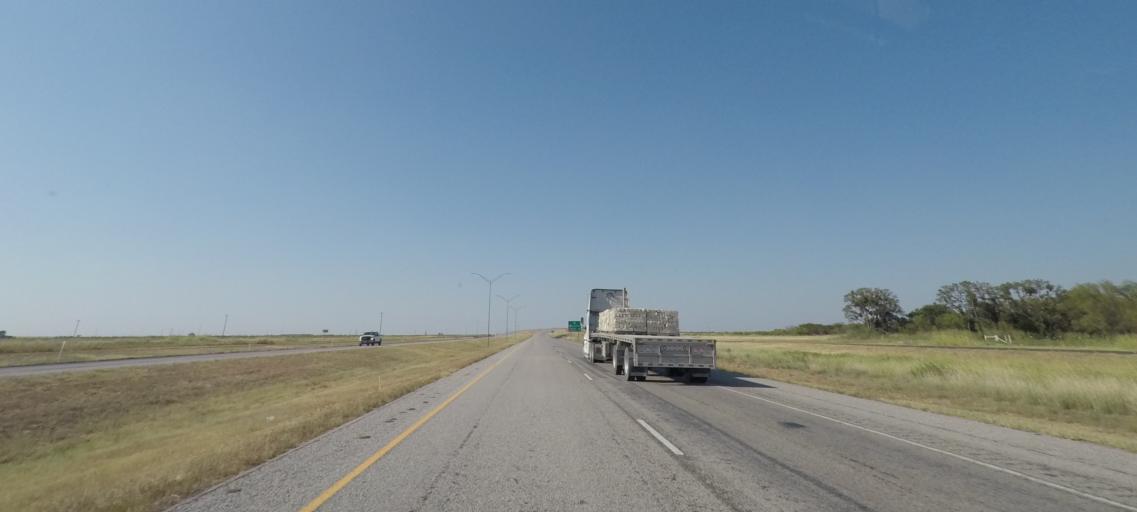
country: US
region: Texas
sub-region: Baylor County
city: Seymour
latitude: 33.6077
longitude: -99.2426
